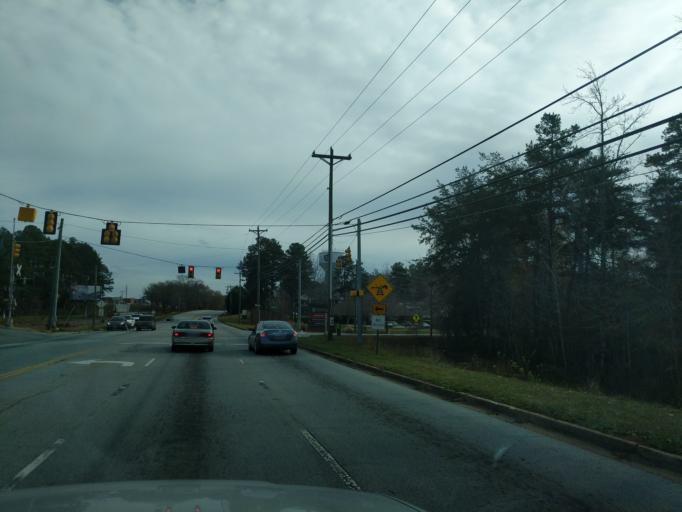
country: US
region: South Carolina
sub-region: Oconee County
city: Seneca
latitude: 34.7011
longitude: -82.9869
